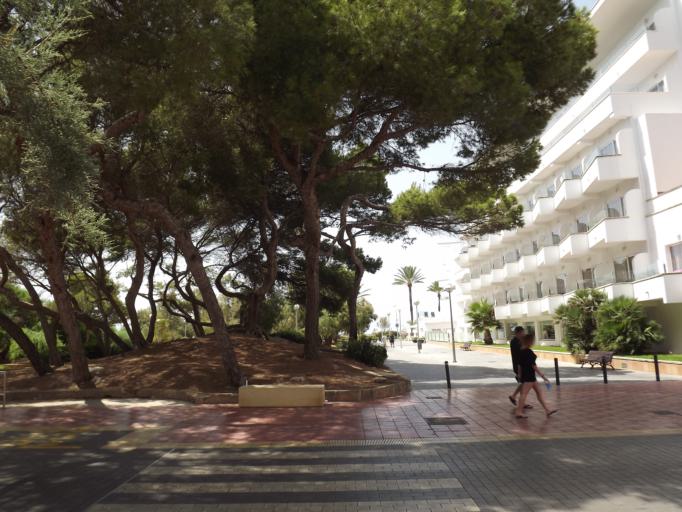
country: ES
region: Balearic Islands
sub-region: Illes Balears
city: s'Arenal
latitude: 39.5221
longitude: 2.7403
